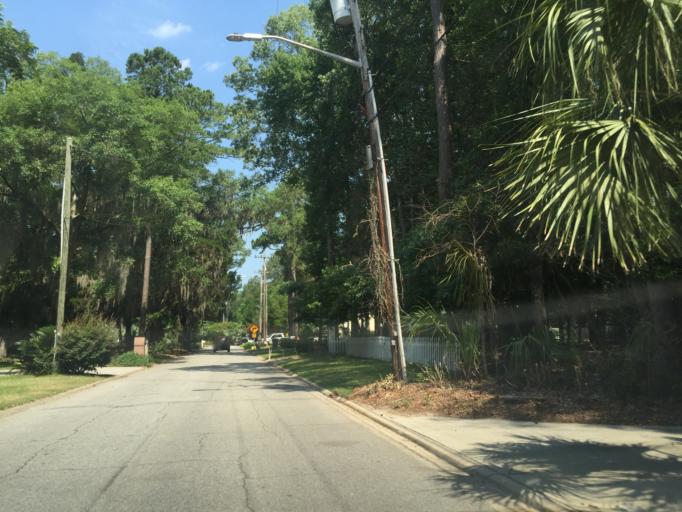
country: US
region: Georgia
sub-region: Chatham County
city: Montgomery
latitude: 31.9689
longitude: -81.1279
